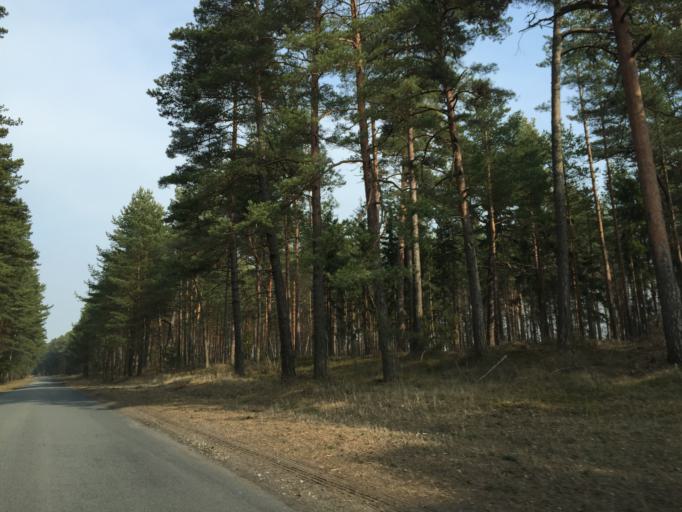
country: LV
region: Salacgrivas
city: Ainazi
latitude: 57.9080
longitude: 24.3810
